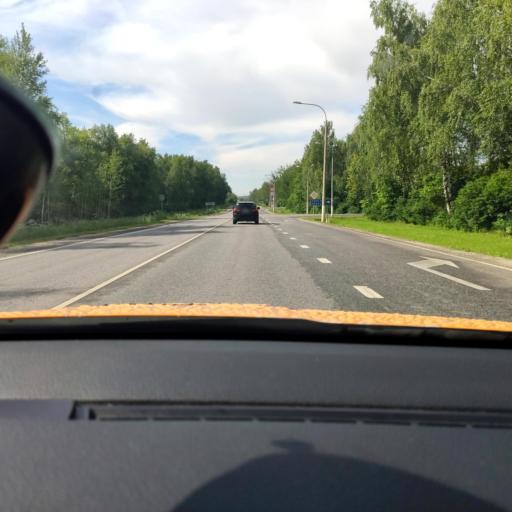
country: RU
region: Moskovskaya
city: Stupino
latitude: 54.9339
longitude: 38.0426
